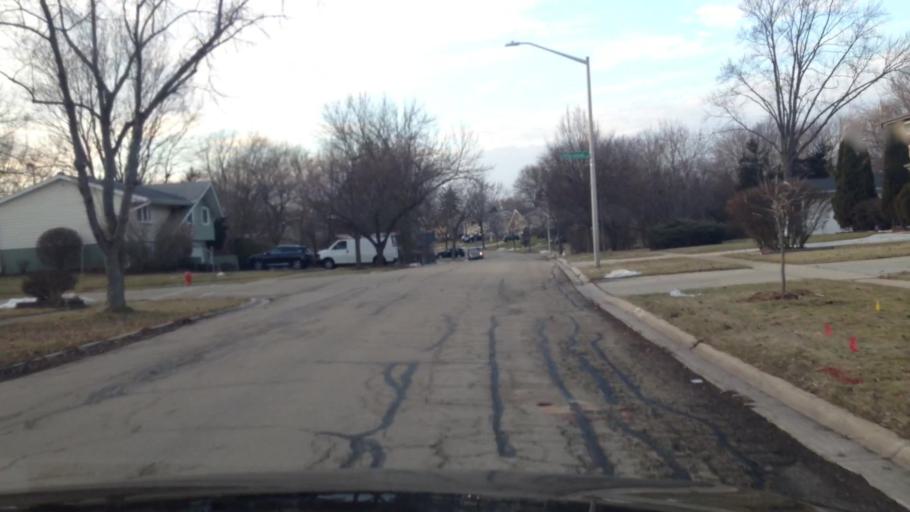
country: US
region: Illinois
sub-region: Cook County
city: Schaumburg
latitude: 42.0159
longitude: -88.1028
